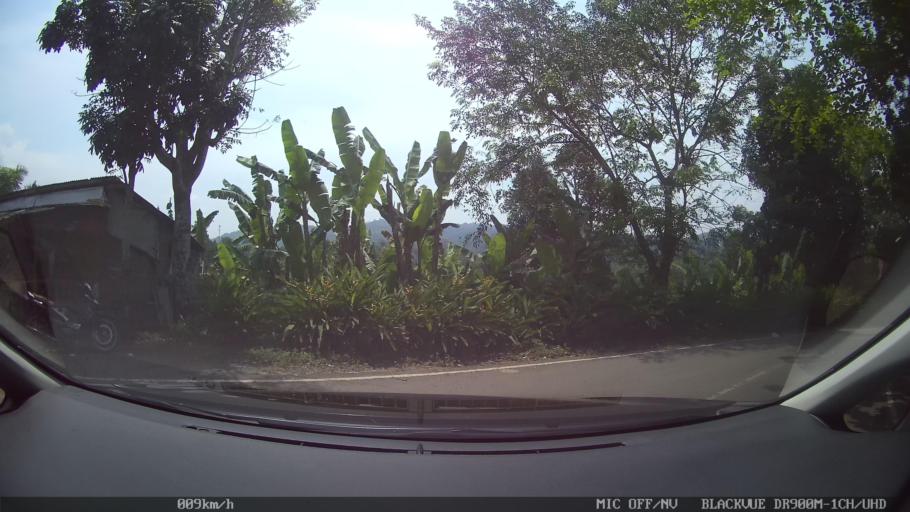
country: ID
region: Lampung
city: Bandarlampung
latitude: -5.4388
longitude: 105.2367
